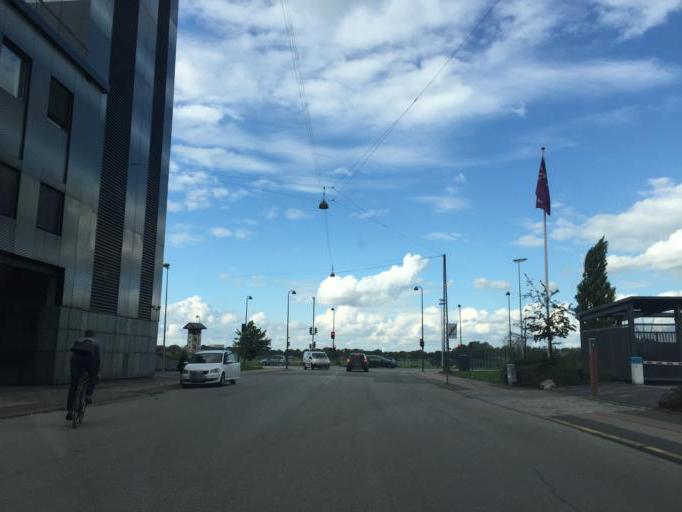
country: DK
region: Capital Region
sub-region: Kobenhavn
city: Christianshavn
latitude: 55.6683
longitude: 12.6194
